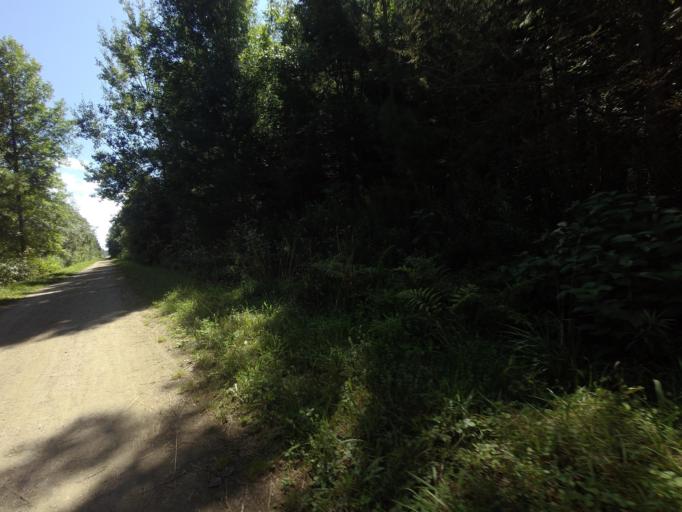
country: CA
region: Ontario
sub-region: Wellington County
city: Guelph
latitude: 43.7363
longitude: -80.3441
